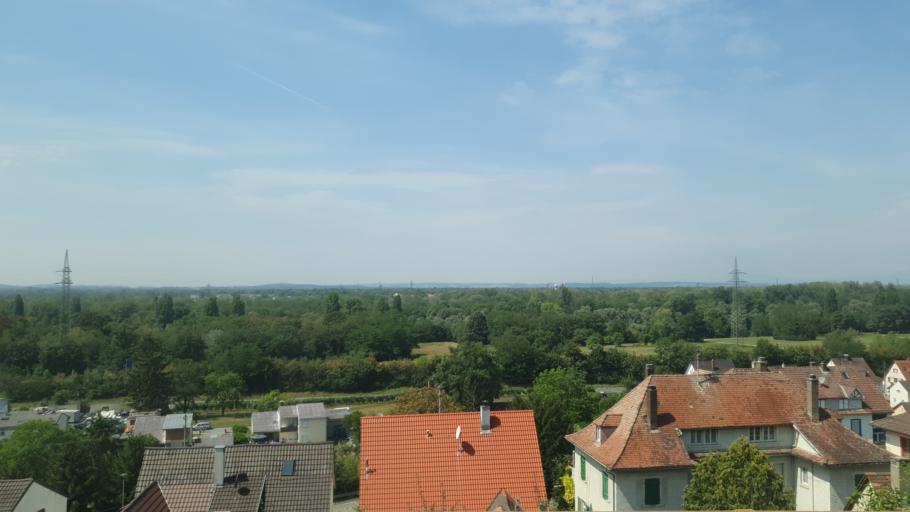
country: FR
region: Alsace
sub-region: Departement du Haut-Rhin
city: Kembs
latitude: 47.6865
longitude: 7.5246
